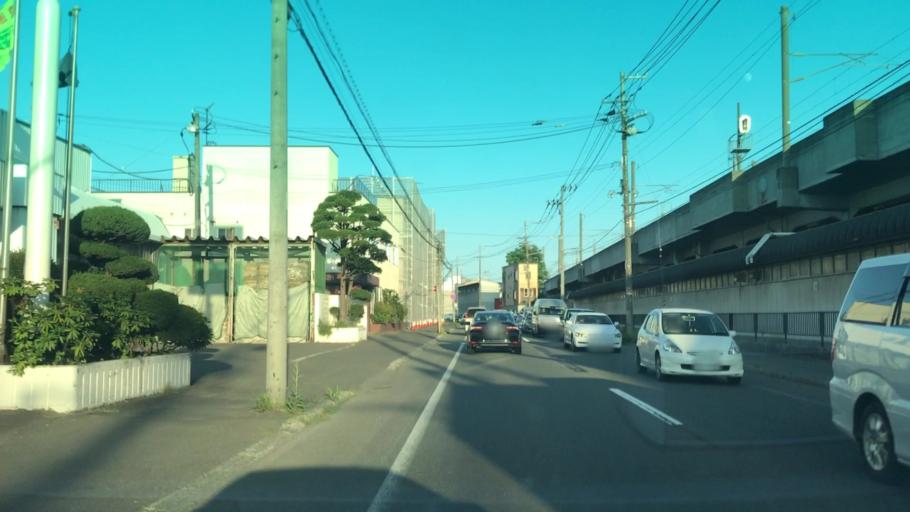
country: JP
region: Hokkaido
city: Sapporo
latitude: 43.0771
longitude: 141.3174
